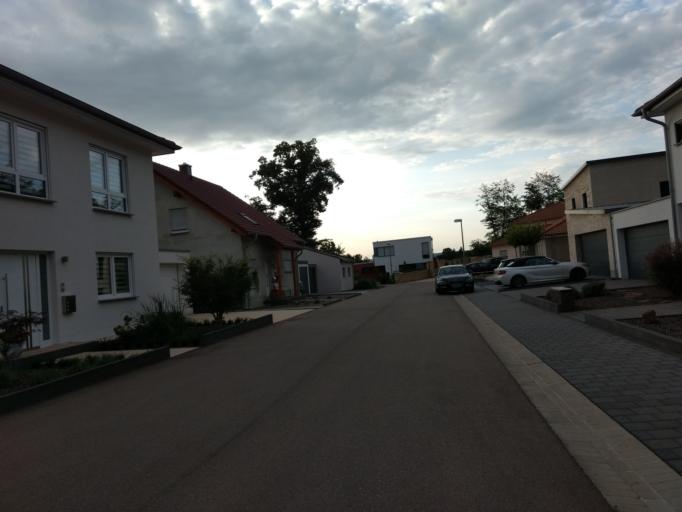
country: DE
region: Saarland
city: Saarwellingen
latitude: 49.3596
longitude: 6.7862
